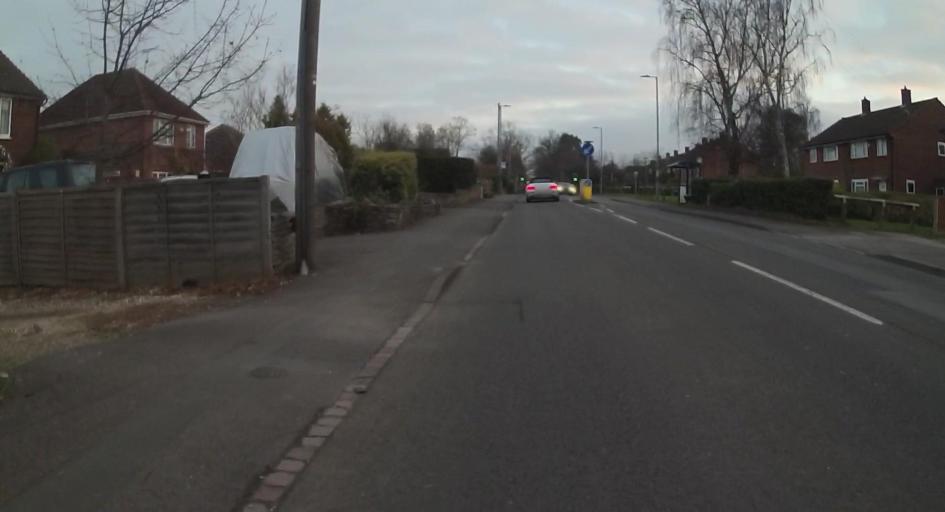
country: GB
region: England
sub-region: Bracknell Forest
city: Bracknell
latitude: 51.4246
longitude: -0.7632
